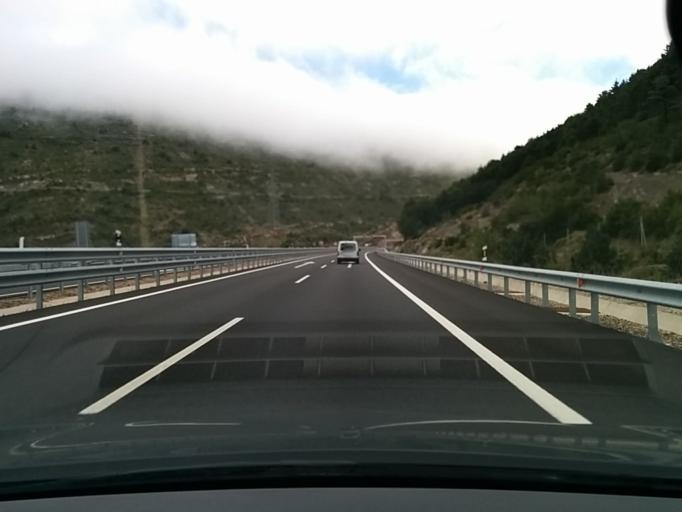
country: ES
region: Aragon
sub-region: Provincia de Huesca
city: Arguis
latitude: 42.3193
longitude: -0.4230
